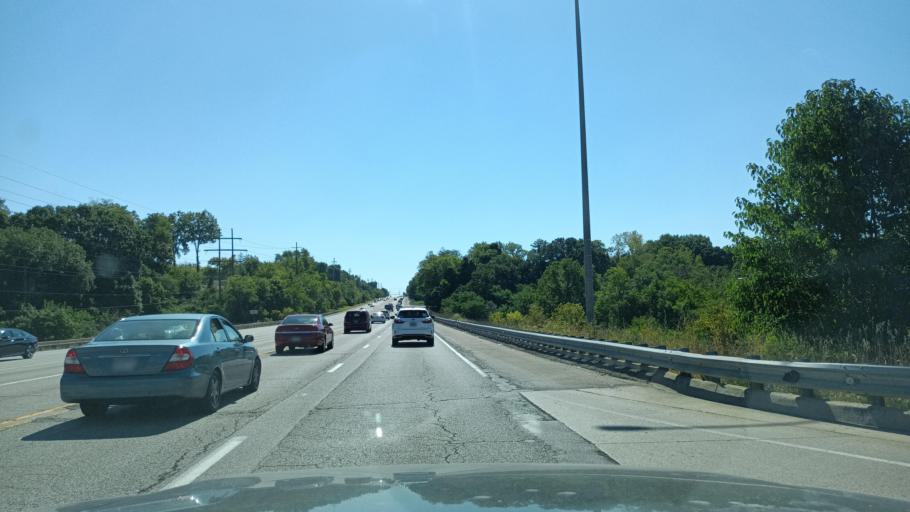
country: US
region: Illinois
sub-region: Peoria County
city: Peoria Heights
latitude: 40.7597
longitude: -89.6389
